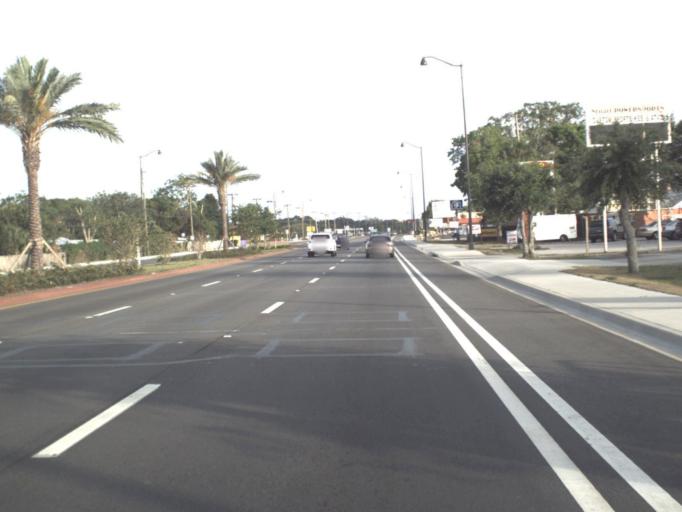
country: US
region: Florida
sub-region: Brevard County
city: Cocoa
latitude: 28.3826
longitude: -80.7416
